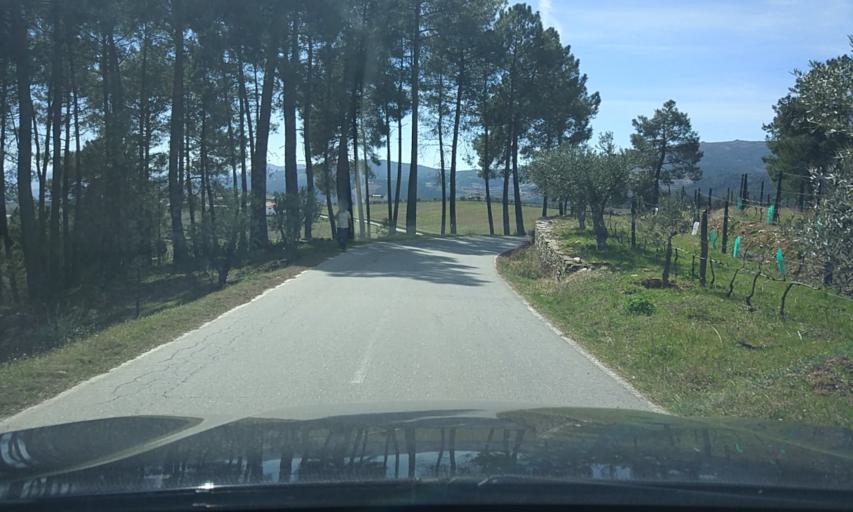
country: PT
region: Vila Real
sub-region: Sabrosa
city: Sabrosa
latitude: 41.3168
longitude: -7.5593
